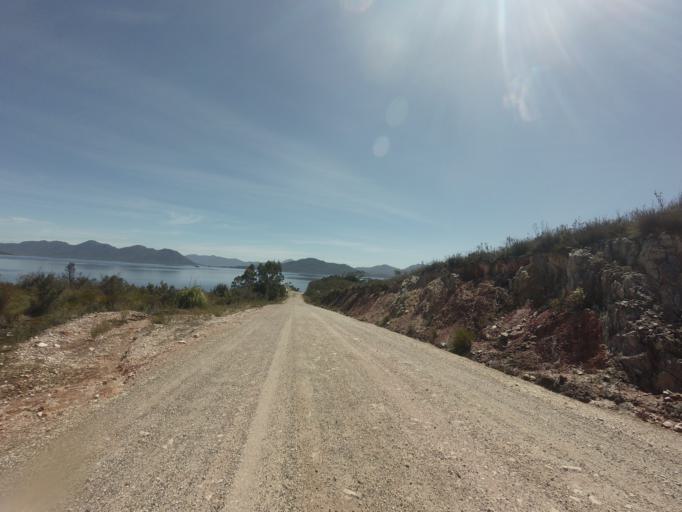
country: AU
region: Tasmania
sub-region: Huon Valley
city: Geeveston
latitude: -43.0299
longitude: 146.3411
